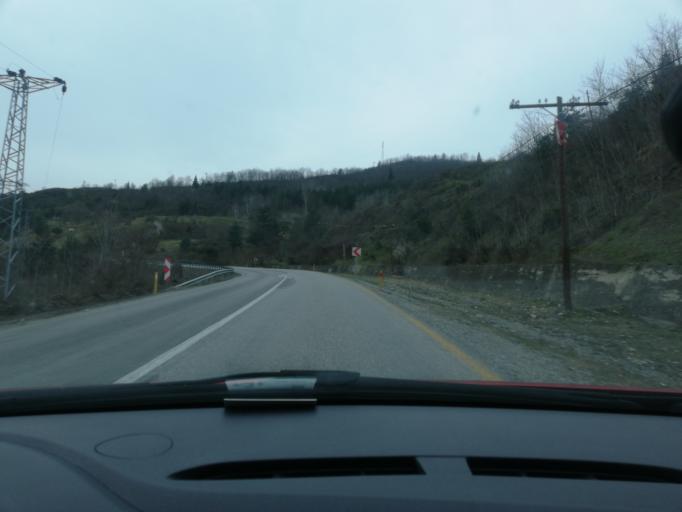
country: TR
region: Kastamonu
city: Inebolu
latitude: 41.9374
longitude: 33.7552
